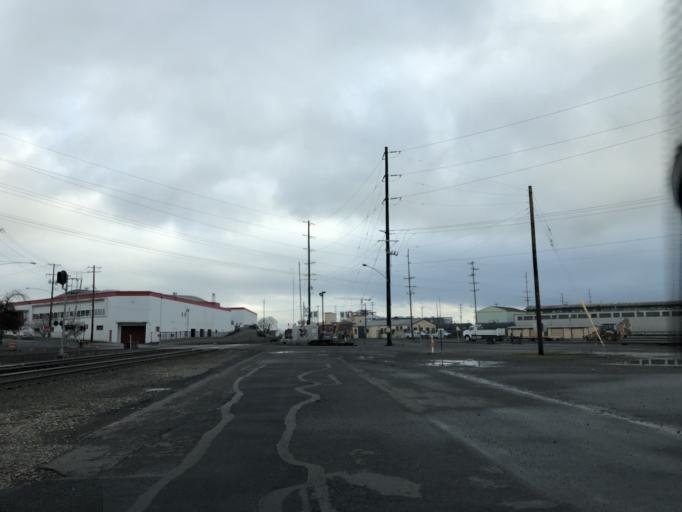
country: US
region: Washington
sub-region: Clark County
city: Vancouver
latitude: 45.6300
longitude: -122.6845
